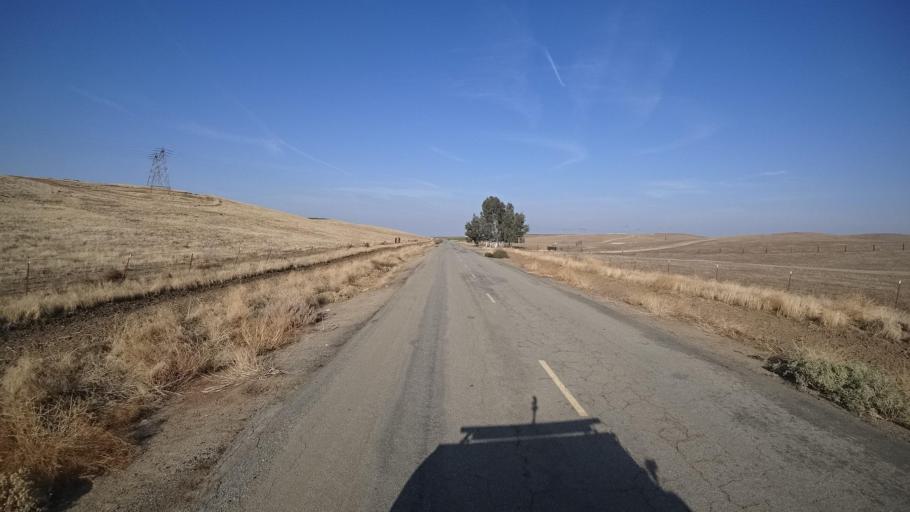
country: US
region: California
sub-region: Tulare County
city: Richgrove
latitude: 35.6382
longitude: -119.0405
